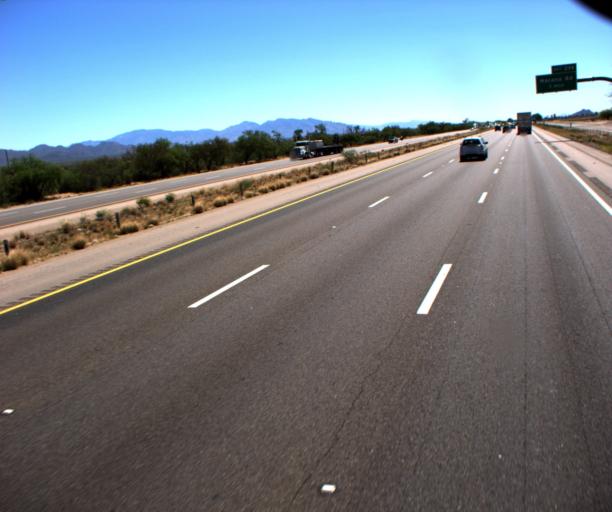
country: US
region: Arizona
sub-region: Pima County
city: Marana
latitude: 32.4764
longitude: -111.2368
